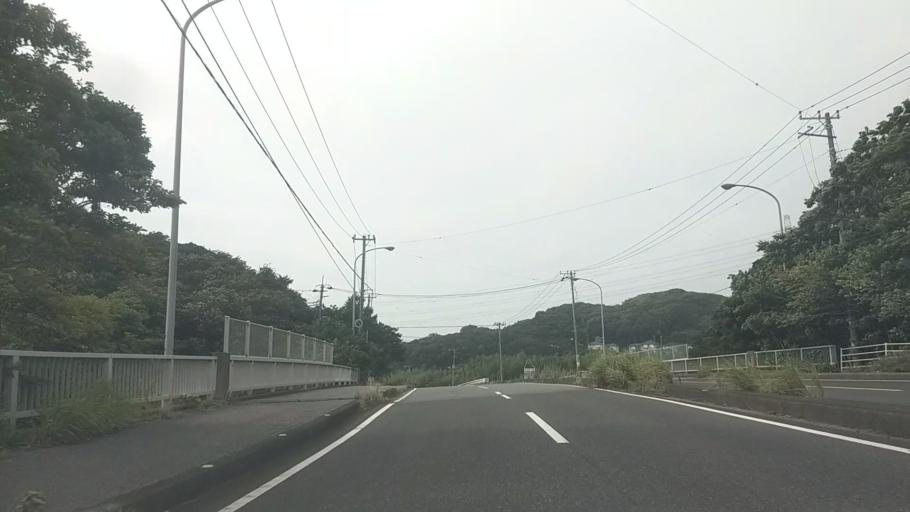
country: JP
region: Chiba
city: Kimitsu
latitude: 35.3400
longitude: 139.8917
